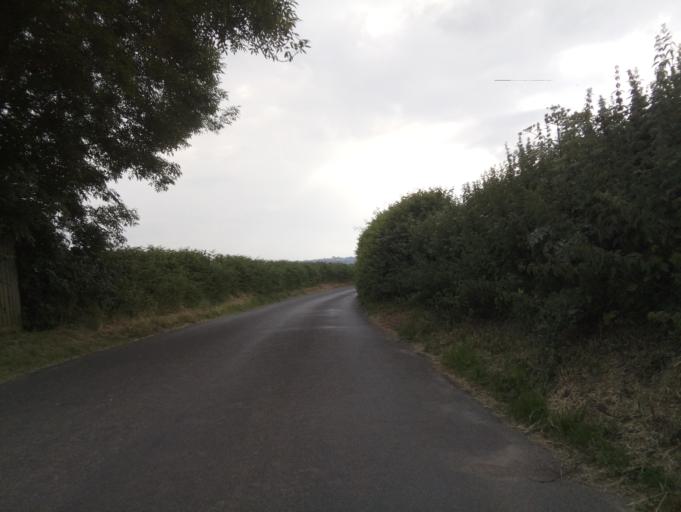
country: GB
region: England
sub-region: Dorset
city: Sherborne
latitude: 50.9782
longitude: -2.5704
